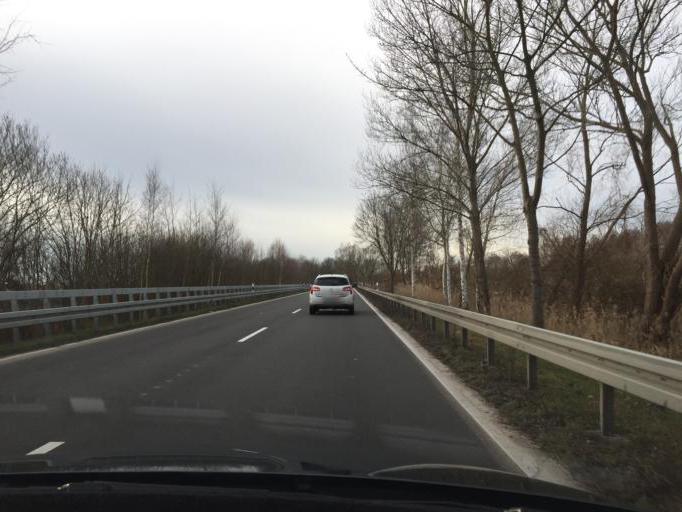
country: DE
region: Brandenburg
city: Peitz
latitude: 51.8473
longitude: 14.3928
